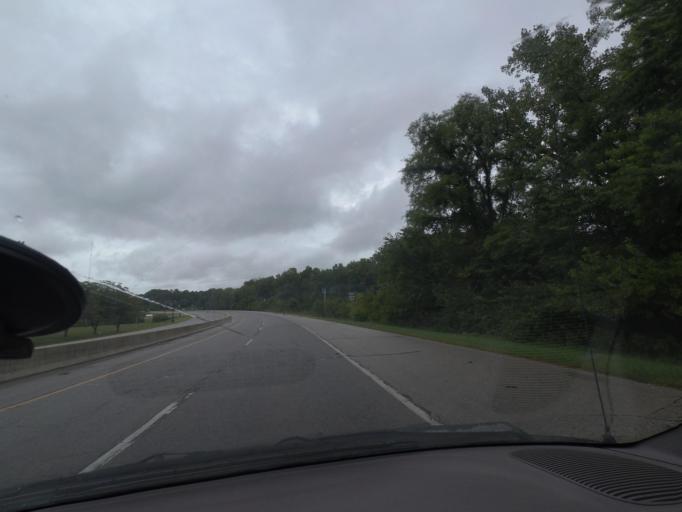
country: US
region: Indiana
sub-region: Montgomery County
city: Crawfordsville
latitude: 40.0495
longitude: -86.9012
